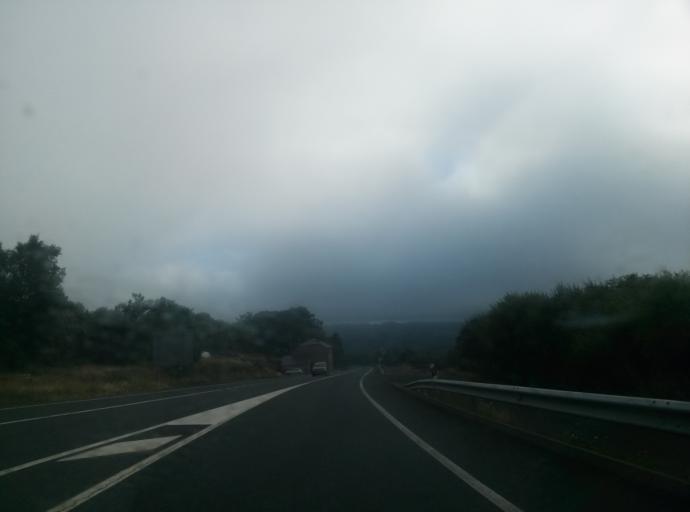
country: ES
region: Galicia
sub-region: Provincia de Lugo
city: Muras
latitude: 43.4657
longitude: -7.7044
